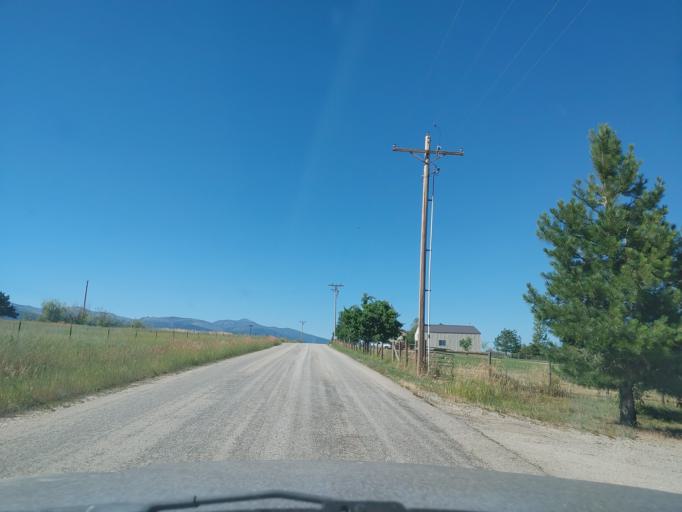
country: US
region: Montana
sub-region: Ravalli County
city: Hamilton
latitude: 46.3146
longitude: -114.2076
